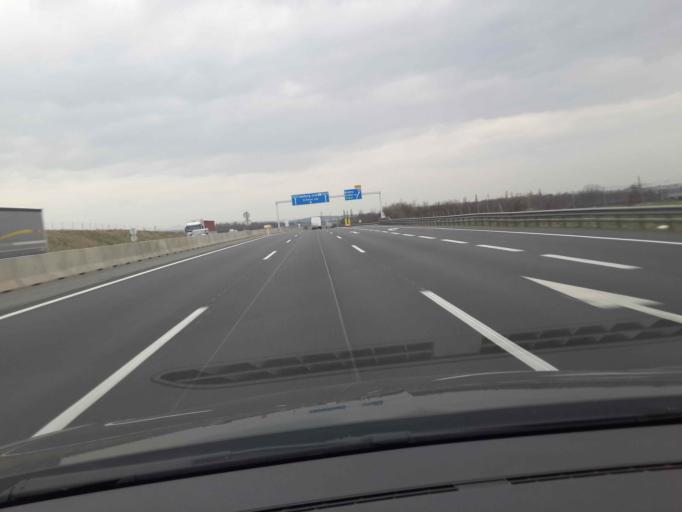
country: AT
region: Lower Austria
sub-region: Politischer Bezirk Sankt Polten
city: Pyhra
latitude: 48.1830
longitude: 15.6716
